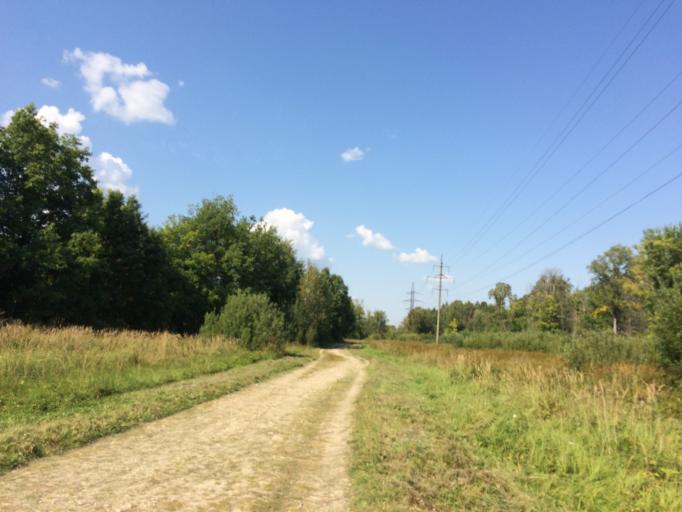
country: RU
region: Mariy-El
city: Yoshkar-Ola
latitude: 56.6159
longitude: 47.9314
